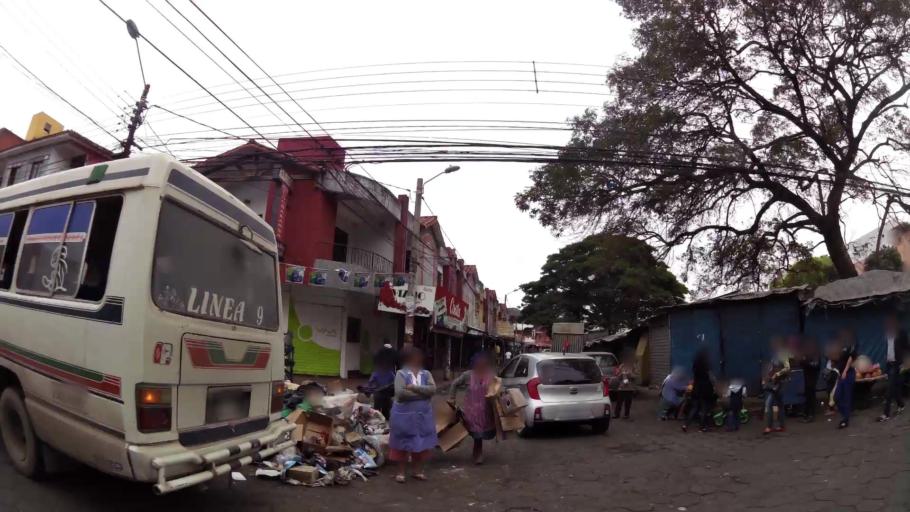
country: BO
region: Santa Cruz
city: Santa Cruz de la Sierra
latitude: -17.7944
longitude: -63.1920
